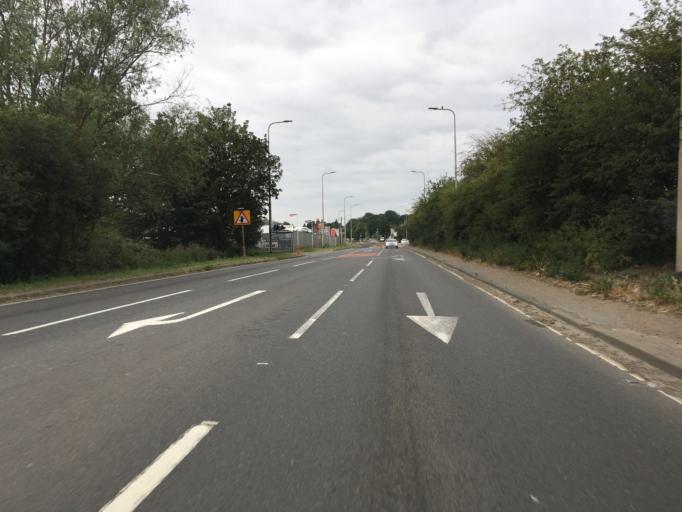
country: GB
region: England
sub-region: Hertfordshire
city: Flamstead
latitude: 51.8222
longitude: -0.4231
